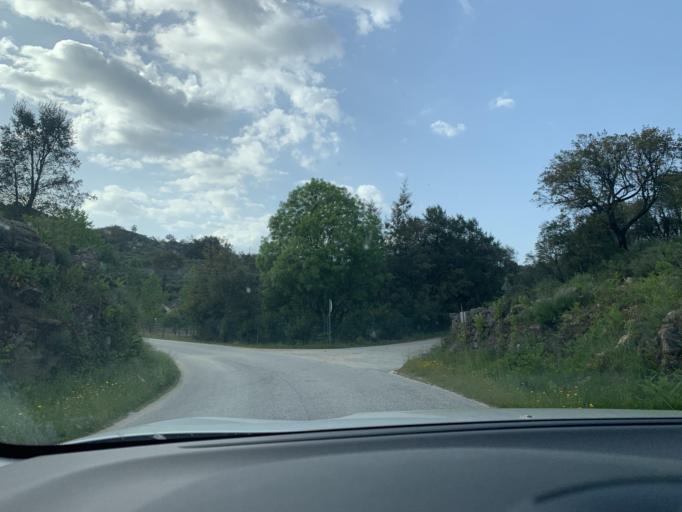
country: PT
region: Guarda
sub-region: Fornos de Algodres
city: Fornos de Algodres
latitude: 40.5752
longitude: -7.5944
